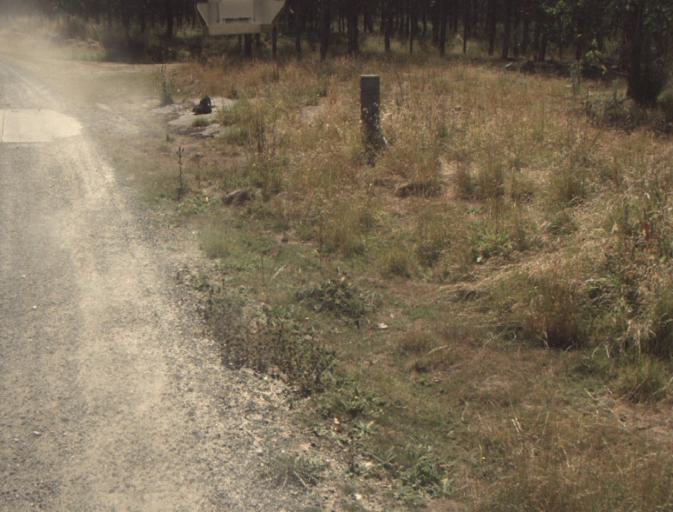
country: AU
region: Tasmania
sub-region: Dorset
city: Scottsdale
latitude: -41.2700
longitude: 147.3518
